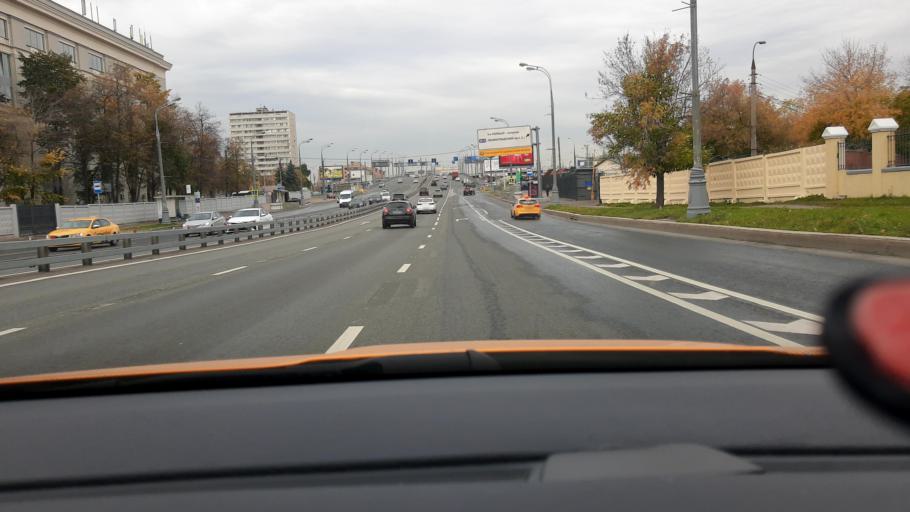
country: RU
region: Moskovskaya
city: Presnenskiy
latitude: 55.7659
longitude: 37.5446
